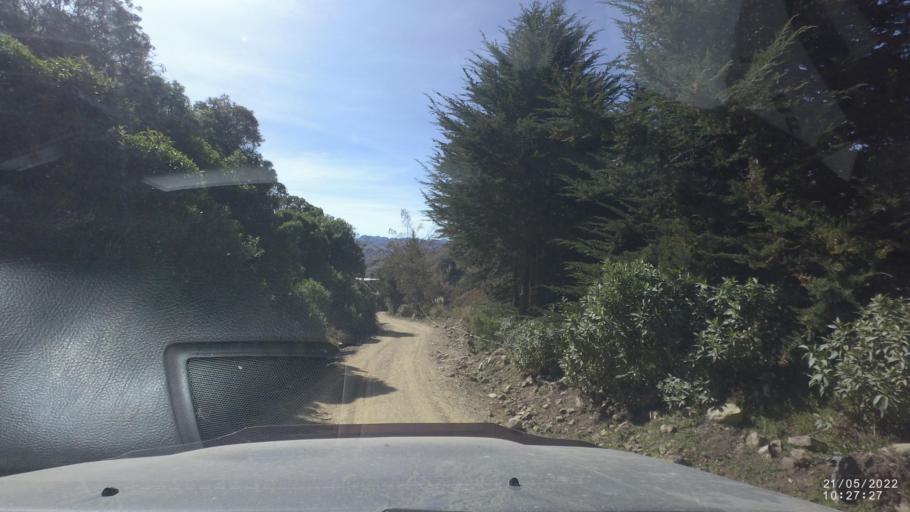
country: BO
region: Cochabamba
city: Colomi
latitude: -17.3233
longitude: -65.9443
